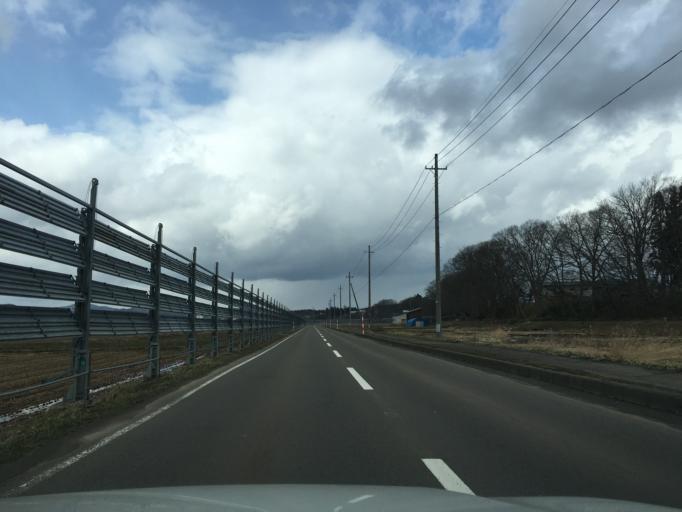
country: JP
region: Akita
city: Takanosu
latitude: 40.1503
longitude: 140.3384
